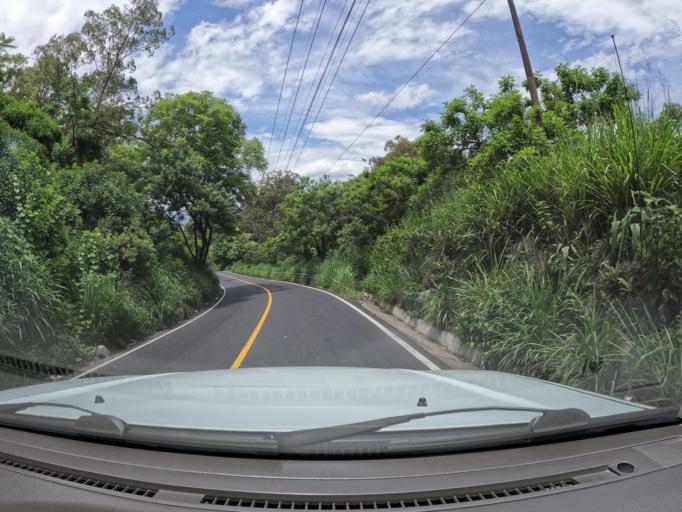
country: GT
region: Guatemala
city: Amatitlan
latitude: 14.4986
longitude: -90.6261
